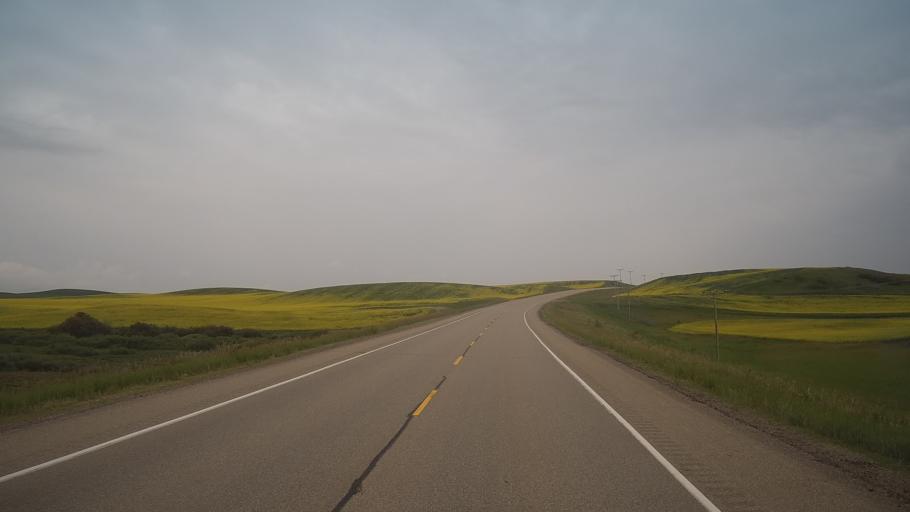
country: CA
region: Saskatchewan
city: Biggar
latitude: 52.0546
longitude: -107.7609
